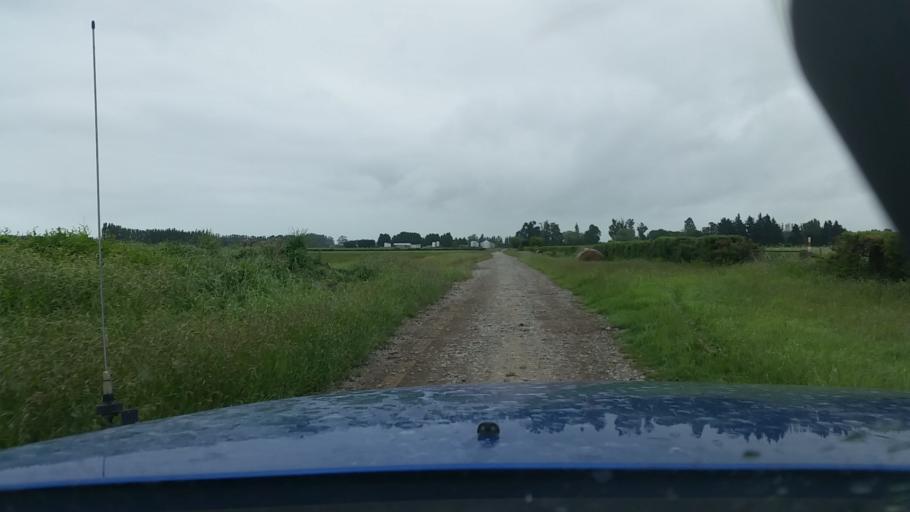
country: NZ
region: Canterbury
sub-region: Ashburton District
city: Tinwald
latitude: -43.9852
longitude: 171.7007
